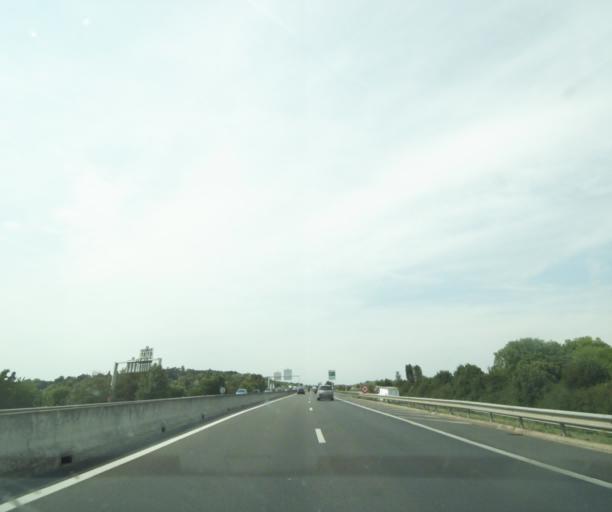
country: FR
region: Centre
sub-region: Departement d'Indre-et-Loire
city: Saint-Cyr-sur-Loire
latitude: 47.3877
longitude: 0.6493
